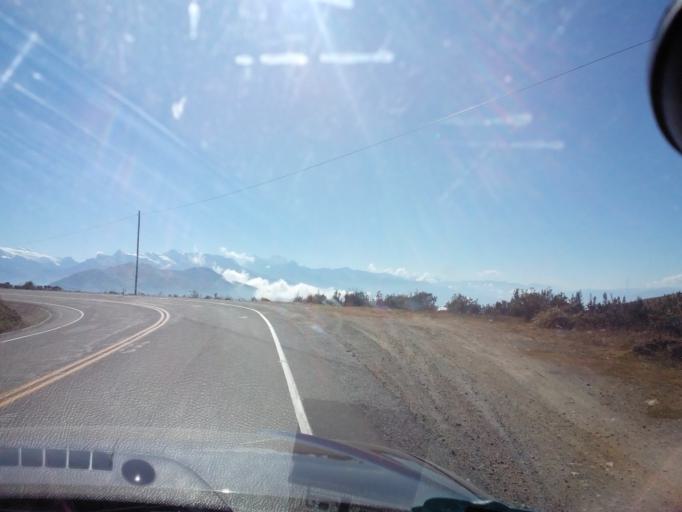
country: PE
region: Apurimac
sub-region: Provincia de Abancay
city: Cachora
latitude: -13.5752
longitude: -72.8196
